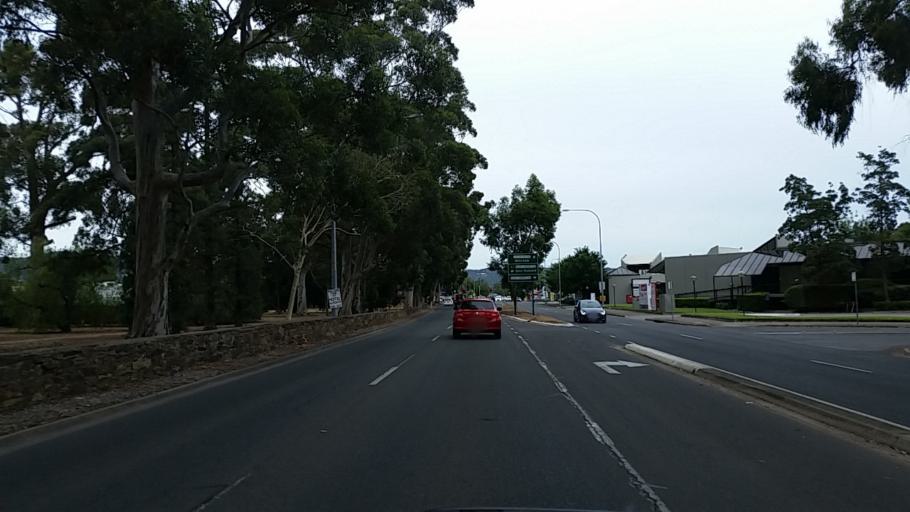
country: AU
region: South Australia
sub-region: Unley
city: Fullarton
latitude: -34.9445
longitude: 138.6249
